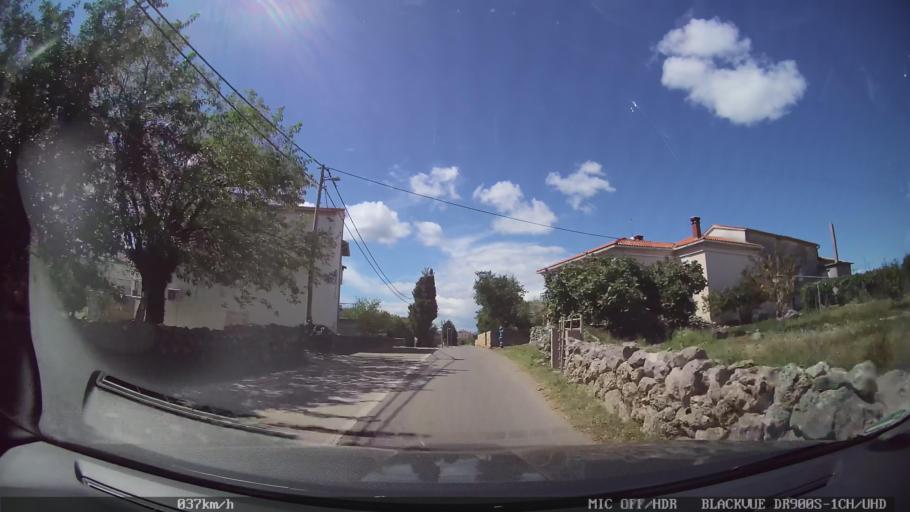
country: HR
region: Primorsko-Goranska
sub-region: Grad Krk
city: Krk
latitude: 45.0507
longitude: 14.5263
